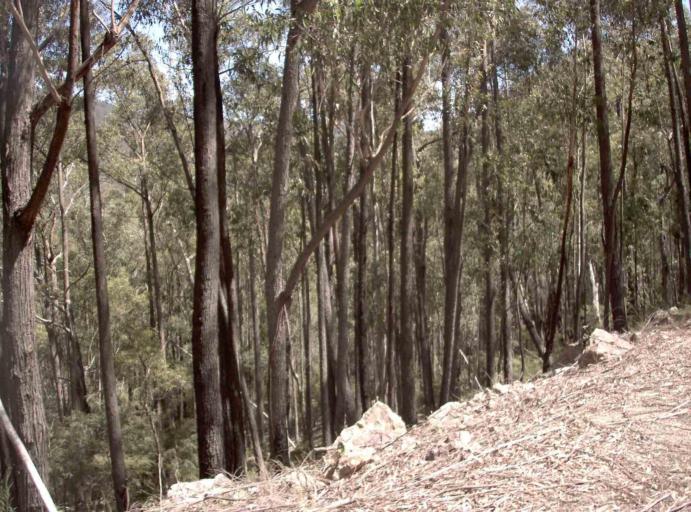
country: AU
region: Victoria
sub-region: East Gippsland
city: Lakes Entrance
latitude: -37.3769
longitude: 148.2167
